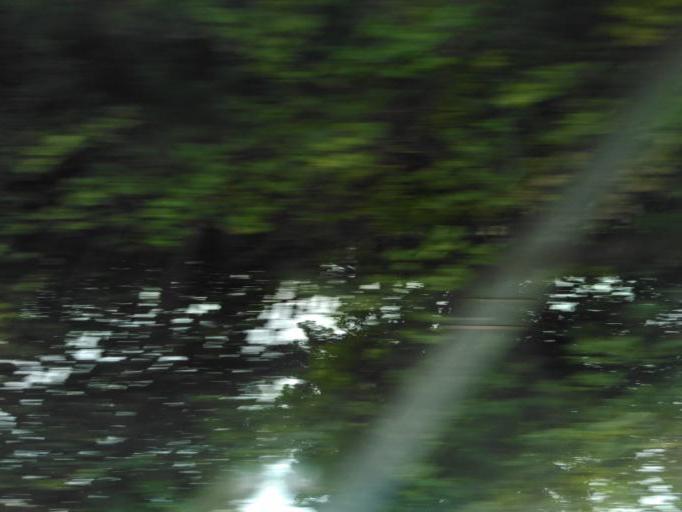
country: GB
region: Scotland
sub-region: East Lothian
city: Musselburgh
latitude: 55.9468
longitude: -3.0995
